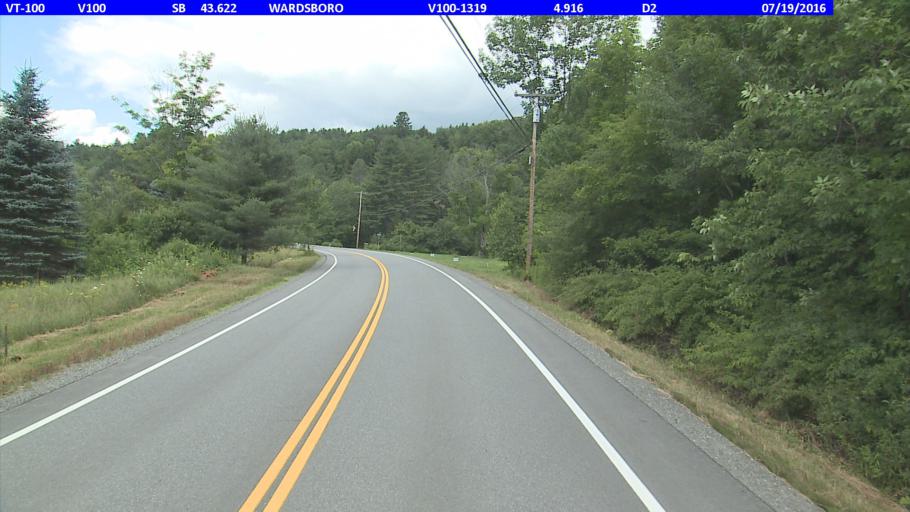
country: US
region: Vermont
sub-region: Windham County
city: Dover
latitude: 43.0692
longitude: -72.8627
